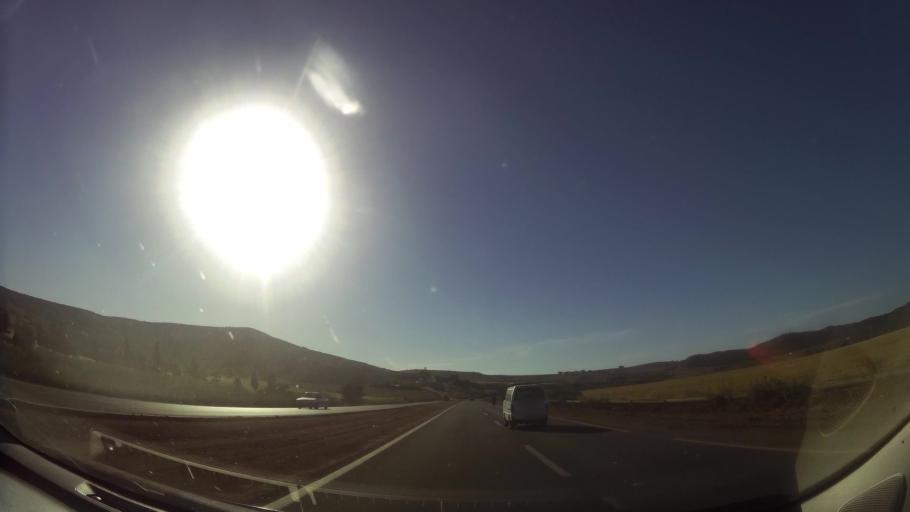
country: MA
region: Oriental
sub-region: Berkane-Taourirt
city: Madagh
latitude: 35.0439
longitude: -2.2148
